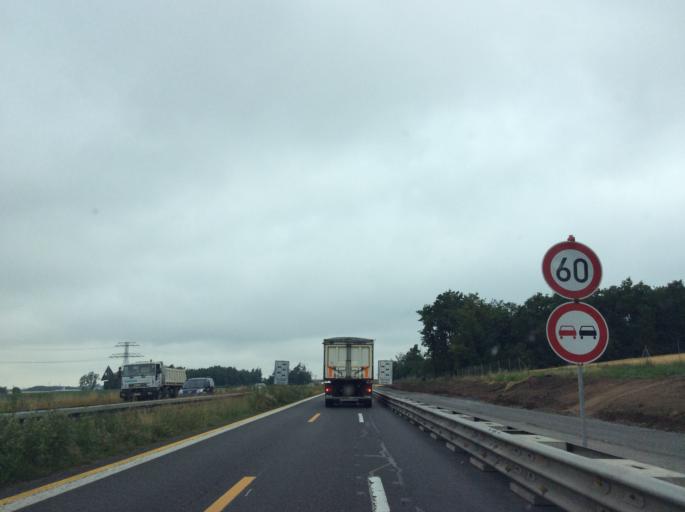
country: DE
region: Saxony
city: Radeburg
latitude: 51.1874
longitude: 13.7438
